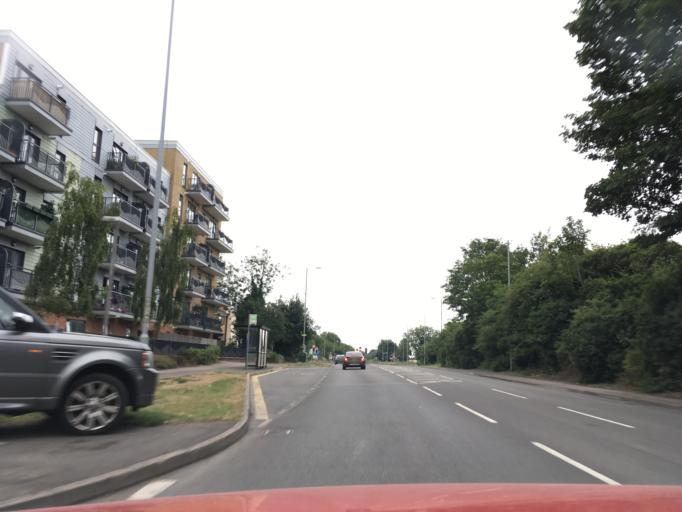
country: GB
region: England
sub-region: Central Bedfordshire
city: Dunstable
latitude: 51.8744
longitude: -0.5034
